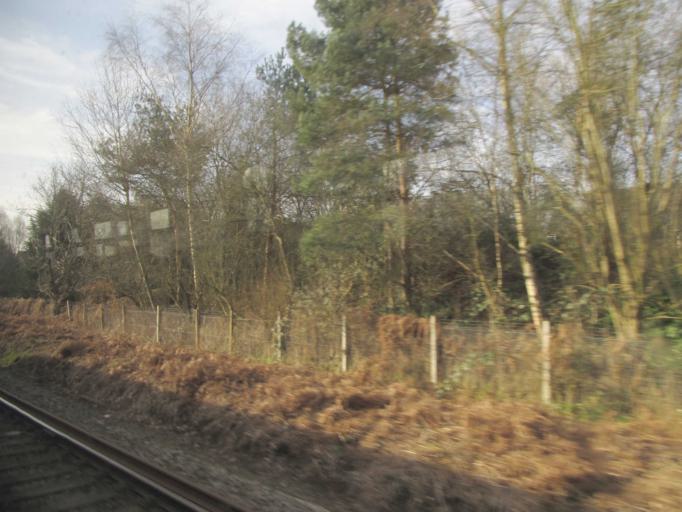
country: GB
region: England
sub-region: Bracknell Forest
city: Sandhurst
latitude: 51.3263
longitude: -0.7715
